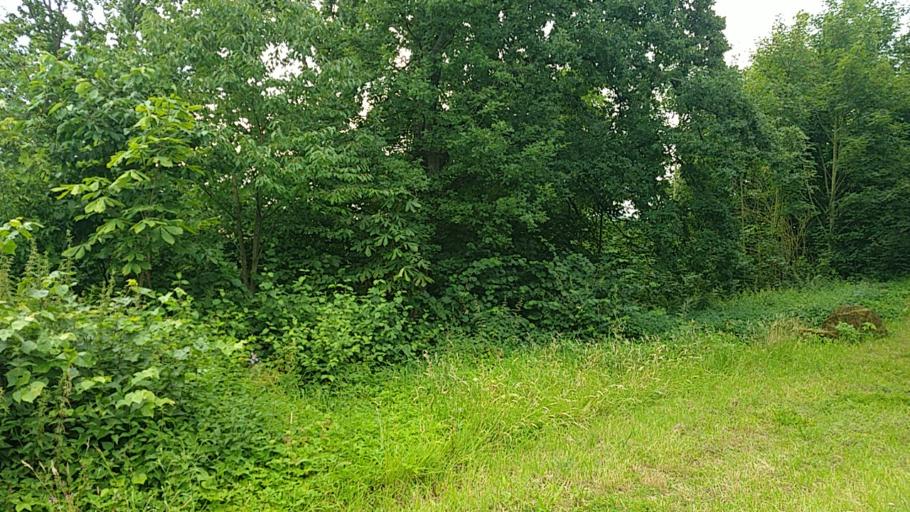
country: DE
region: Lower Saxony
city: Dassel
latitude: 51.7664
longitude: 9.7560
